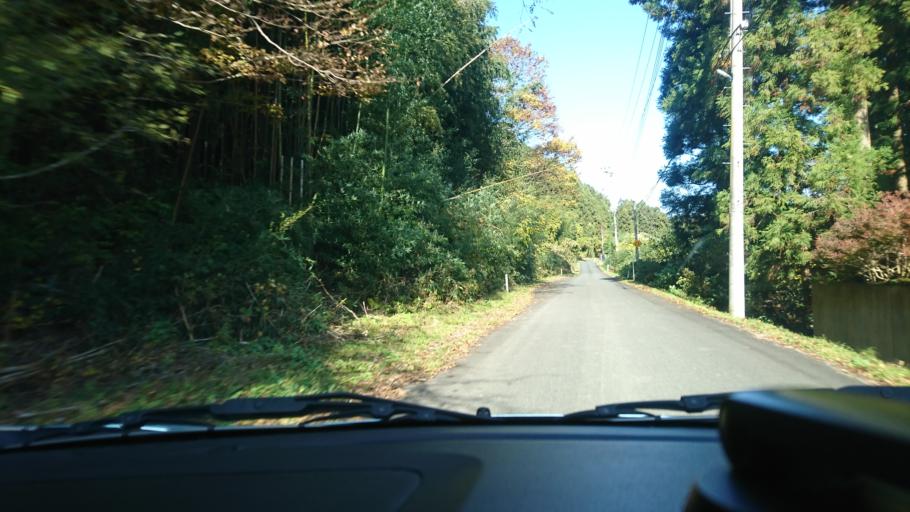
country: JP
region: Iwate
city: Ichinoseki
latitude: 38.8168
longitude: 141.2503
